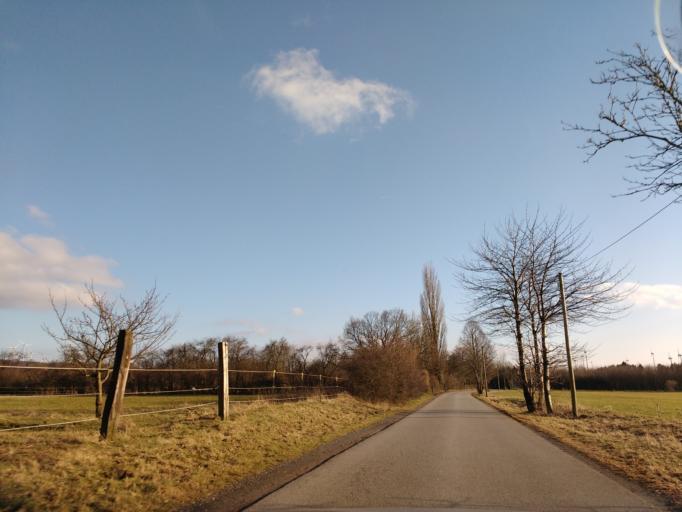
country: DE
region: North Rhine-Westphalia
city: Bad Lippspringe
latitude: 51.7539
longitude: 8.8427
